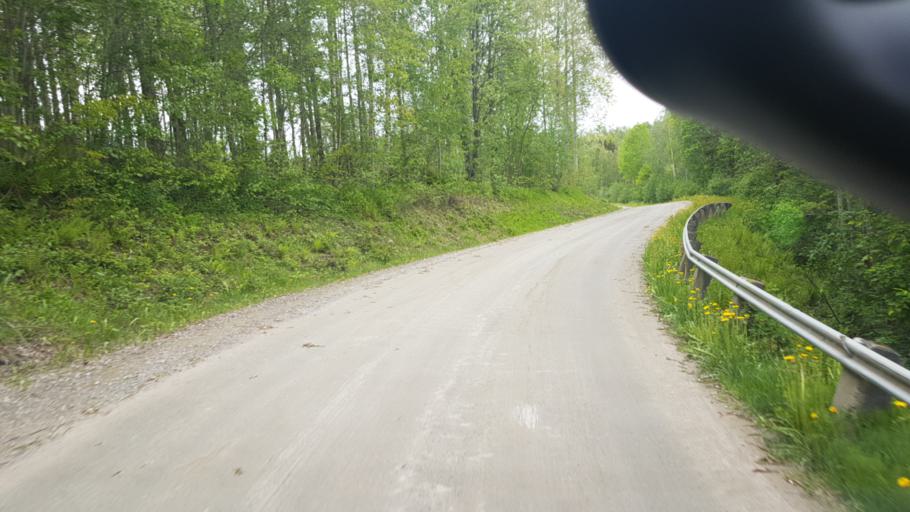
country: SE
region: Vaermland
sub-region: Arvika Kommun
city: Arvika
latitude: 59.8195
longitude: 12.5550
